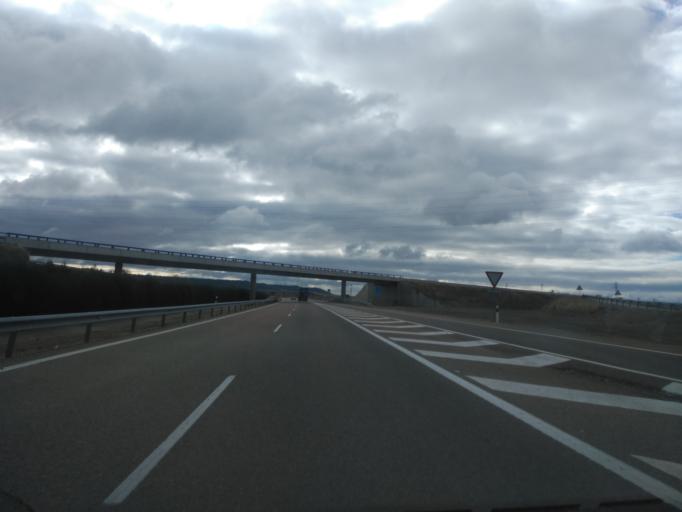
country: ES
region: Castille and Leon
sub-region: Provincia de Palencia
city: Fuentes de Valdepero
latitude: 42.0618
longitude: -4.4929
